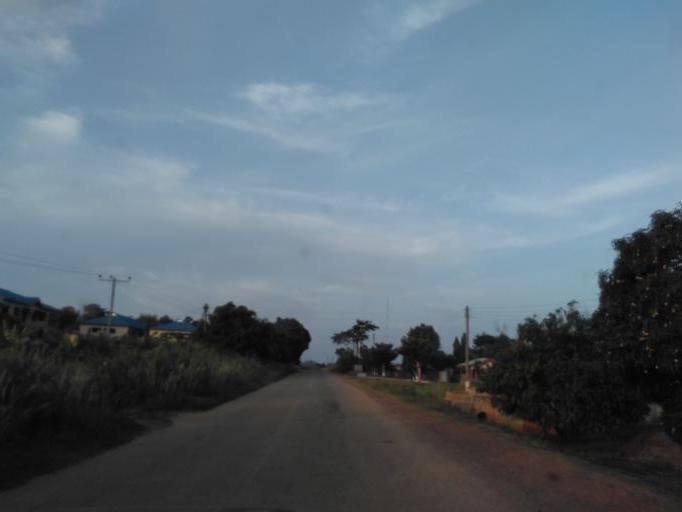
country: GH
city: Bekwai
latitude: 6.5401
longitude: -1.4543
